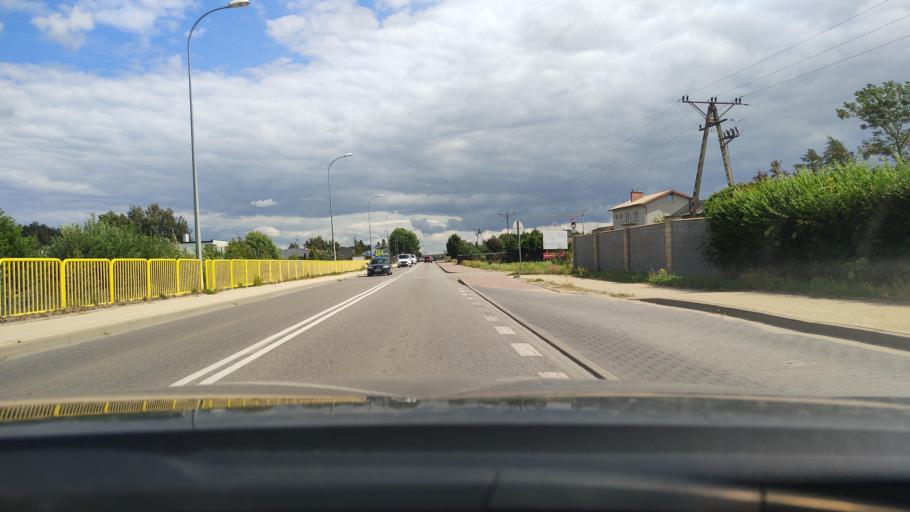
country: PL
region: Pomeranian Voivodeship
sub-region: Powiat wejherowski
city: Bojano
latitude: 54.4769
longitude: 18.3683
